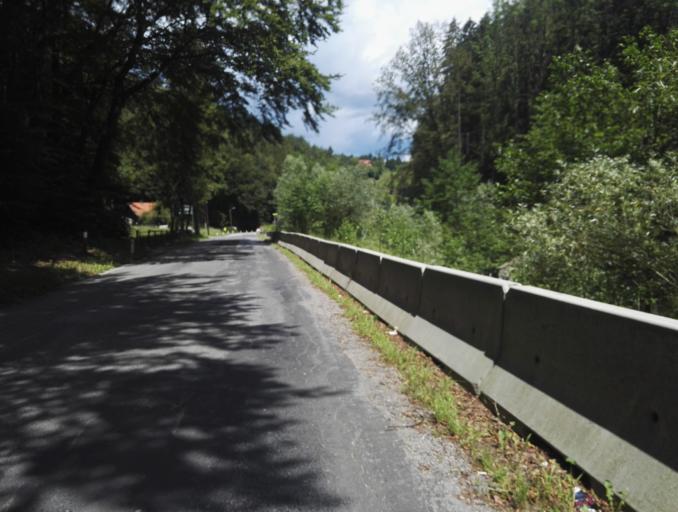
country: AT
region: Styria
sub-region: Politischer Bezirk Graz-Umgebung
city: Gratwein
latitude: 47.1023
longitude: 15.3156
